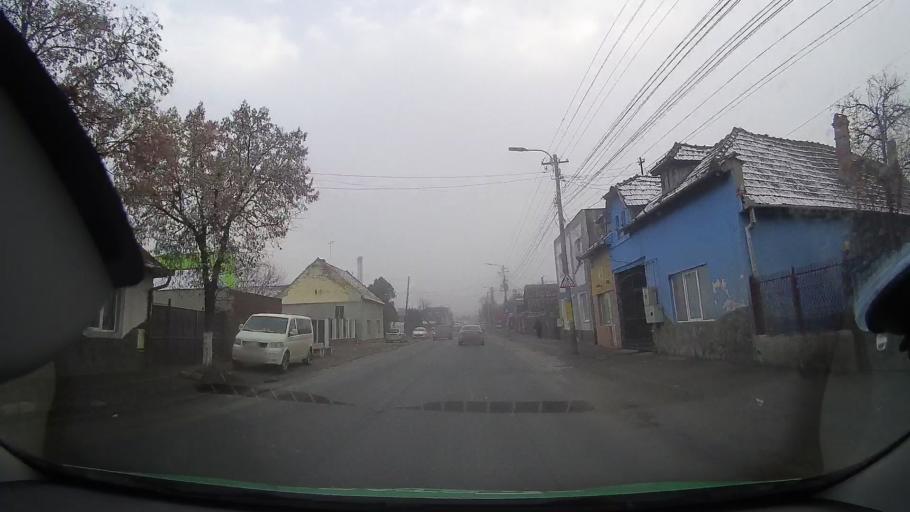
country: RO
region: Mures
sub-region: Municipiul Tarnaveni
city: Tarnaveni
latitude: 46.3186
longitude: 24.2966
